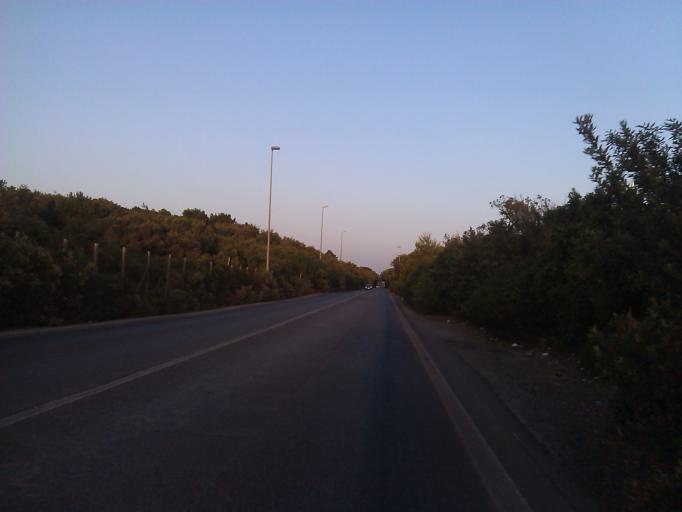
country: IT
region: Latium
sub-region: Citta metropolitana di Roma Capitale
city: Acilia-Castel Fusano-Ostia Antica
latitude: 41.7097
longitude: 12.3316
